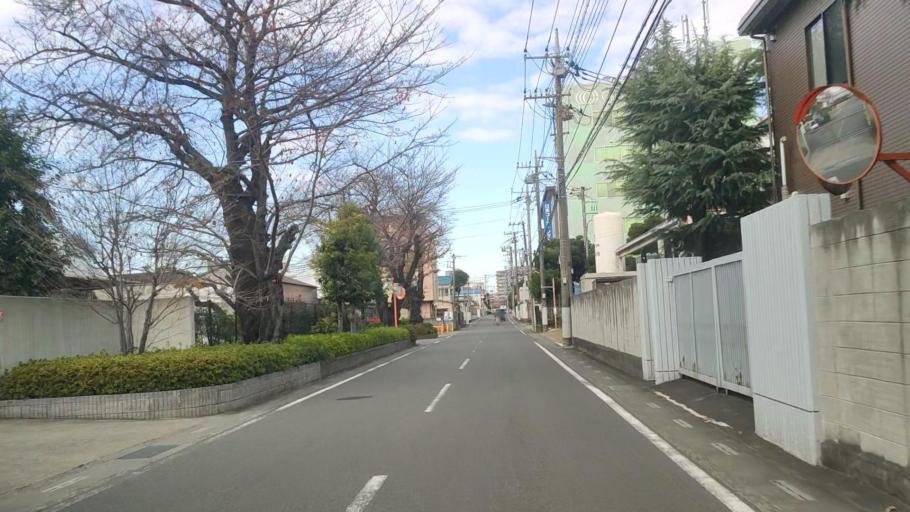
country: JP
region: Kanagawa
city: Minami-rinkan
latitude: 35.4990
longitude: 139.4314
